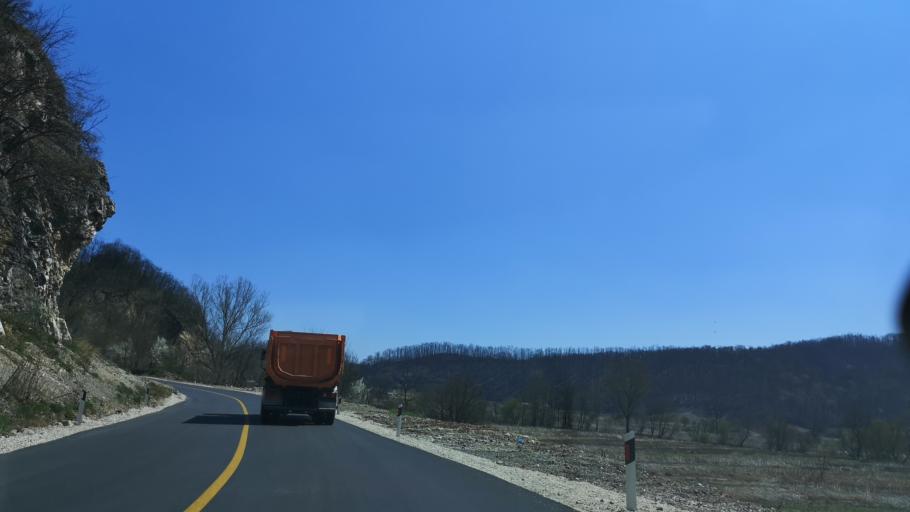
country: RS
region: Central Serbia
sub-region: Moravicki Okrug
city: Lucani
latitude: 43.8709
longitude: 20.1144
